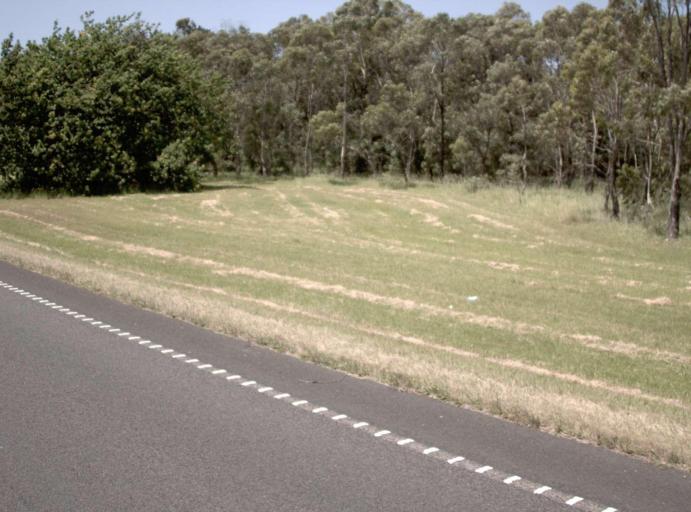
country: AU
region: Victoria
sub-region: Cardinia
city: Garfield
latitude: -38.0699
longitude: 145.6297
